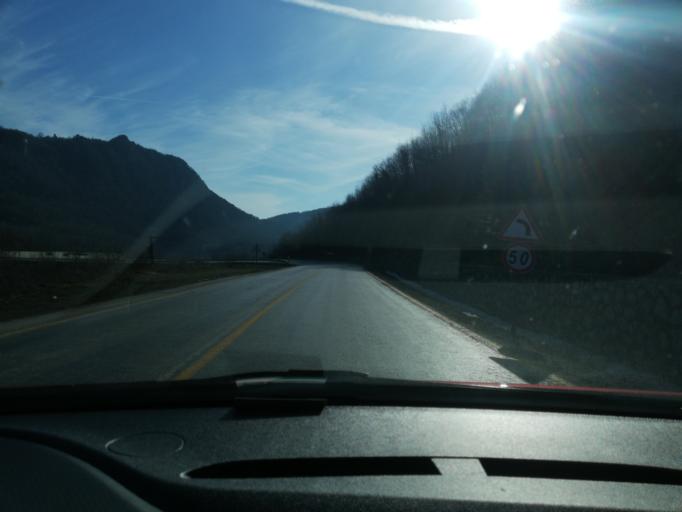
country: TR
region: Kastamonu
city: Cide
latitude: 41.8632
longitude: 33.0524
